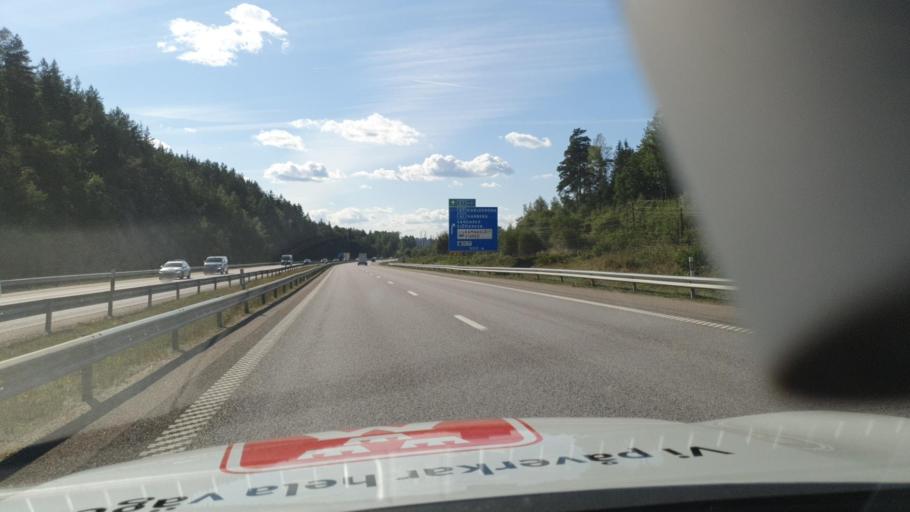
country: SE
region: Vaestra Goetaland
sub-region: Boras Kommun
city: Boras
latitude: 57.7140
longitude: 12.8880
